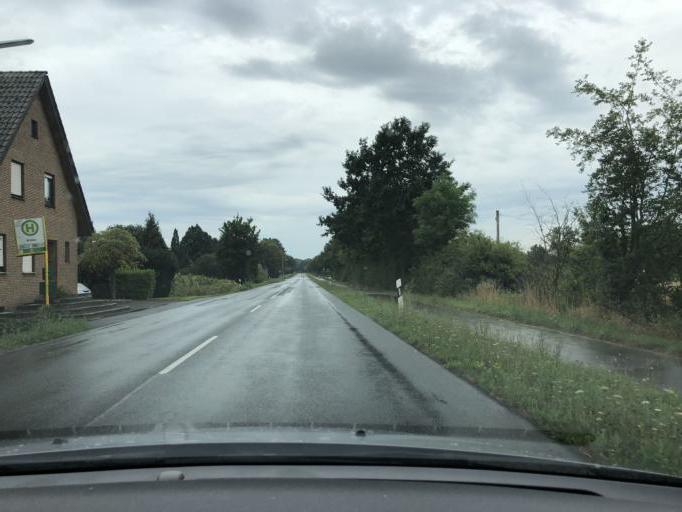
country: DE
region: North Rhine-Westphalia
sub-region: Regierungsbezirk Dusseldorf
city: Schermbeck
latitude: 51.7138
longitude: 6.8735
